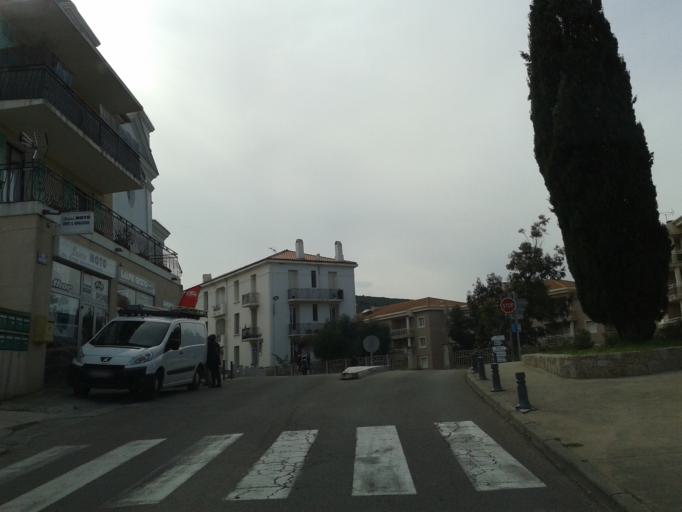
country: FR
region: Corsica
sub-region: Departement de la Haute-Corse
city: L'Ile-Rousse
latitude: 42.6346
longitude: 8.9362
